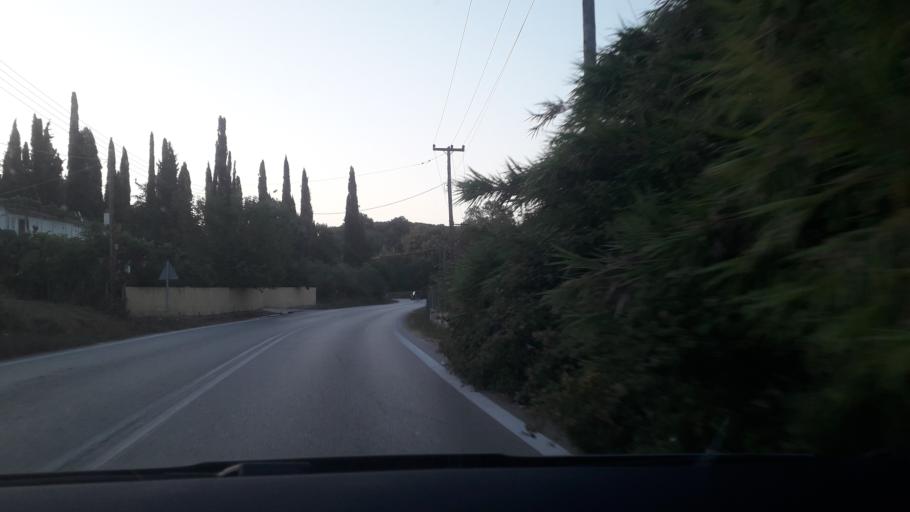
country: GR
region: Ionian Islands
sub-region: Nomos Kerkyras
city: Agios Matthaios
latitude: 39.4774
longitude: 19.9183
